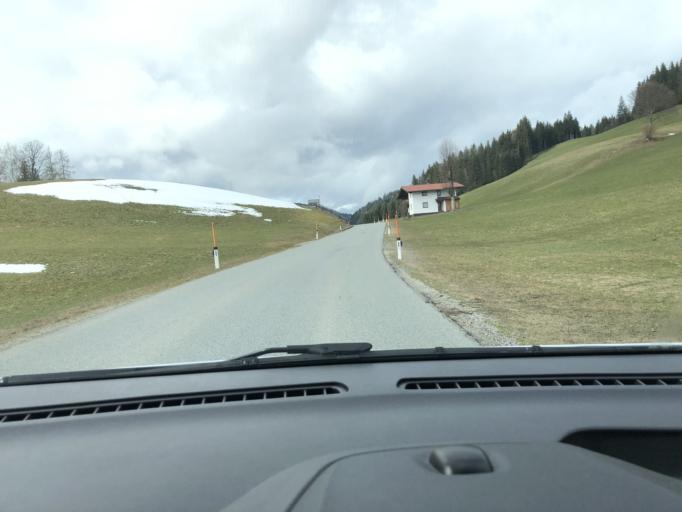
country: AT
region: Tyrol
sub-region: Politischer Bezirk Kitzbuhel
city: Itter
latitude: 47.4473
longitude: 12.1279
